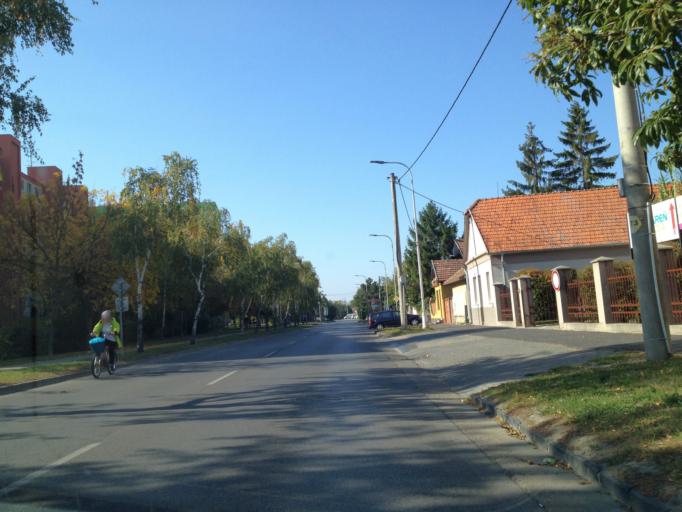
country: SK
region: Nitriansky
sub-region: Okres Nove Zamky
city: Nove Zamky
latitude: 47.9835
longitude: 18.1535
